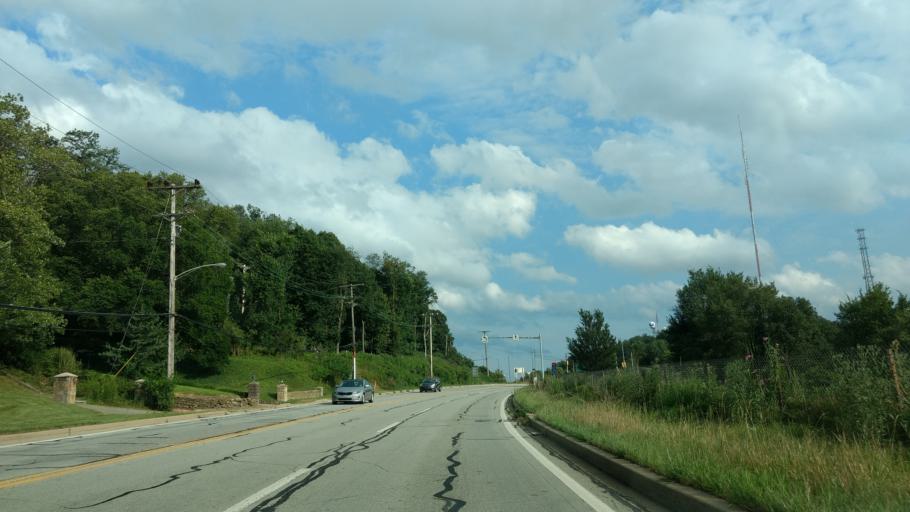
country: US
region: Pennsylvania
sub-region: Allegheny County
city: West View
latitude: 40.4998
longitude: -80.0214
